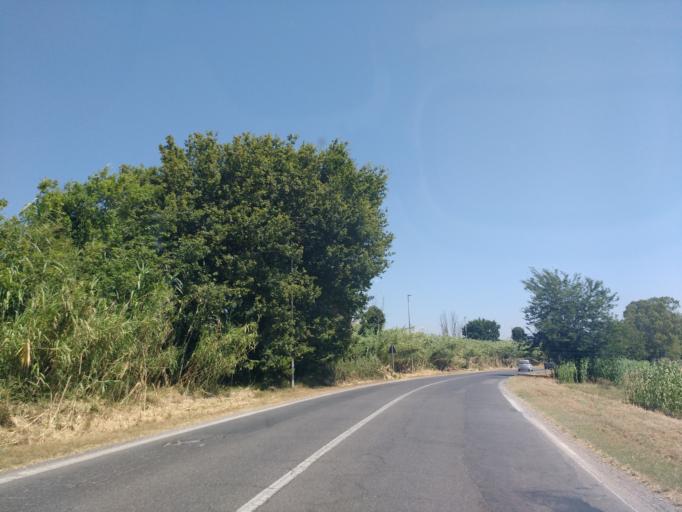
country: IT
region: Latium
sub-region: Citta metropolitana di Roma Capitale
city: Maccarese
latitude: 41.8735
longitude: 12.2094
